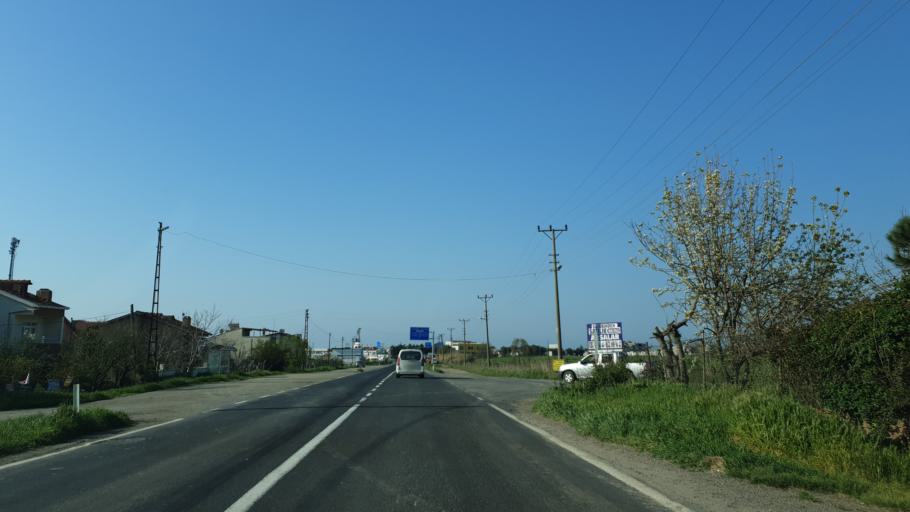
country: TR
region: Tekirdag
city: Corlu
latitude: 41.0133
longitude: 27.7182
